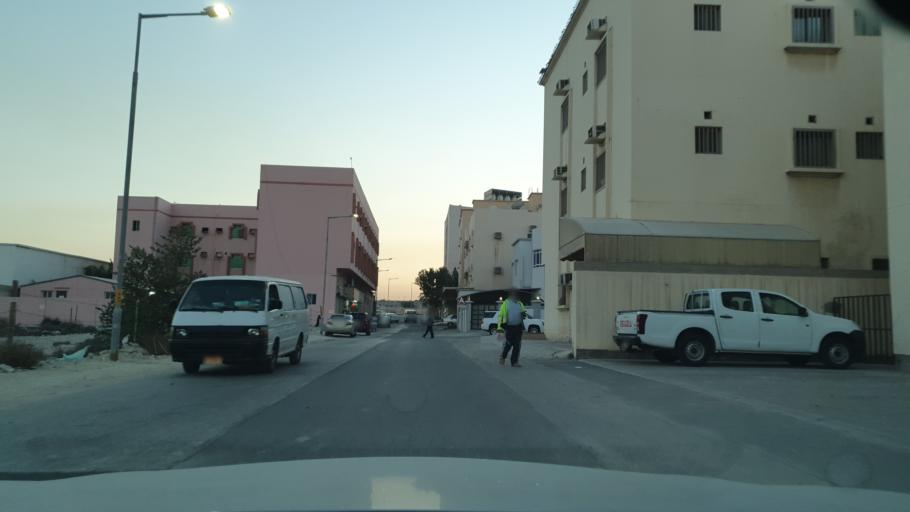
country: BH
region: Northern
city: Ar Rifa'
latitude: 26.1202
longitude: 50.5843
